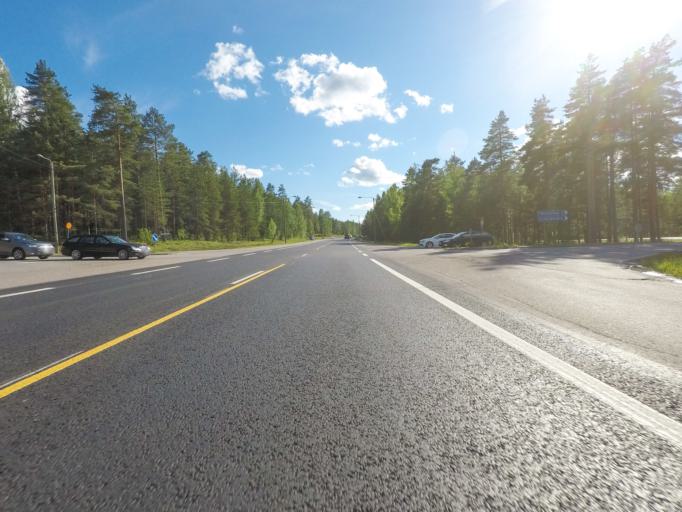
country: FI
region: Uusimaa
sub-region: Helsinki
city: Vihti
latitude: 60.3429
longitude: 24.3073
